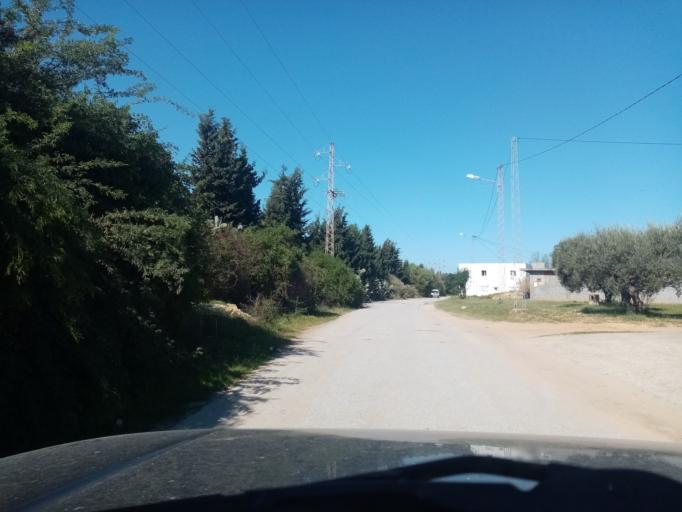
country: TN
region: Nabul
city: Bu `Urqub
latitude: 36.5693
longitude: 10.5778
